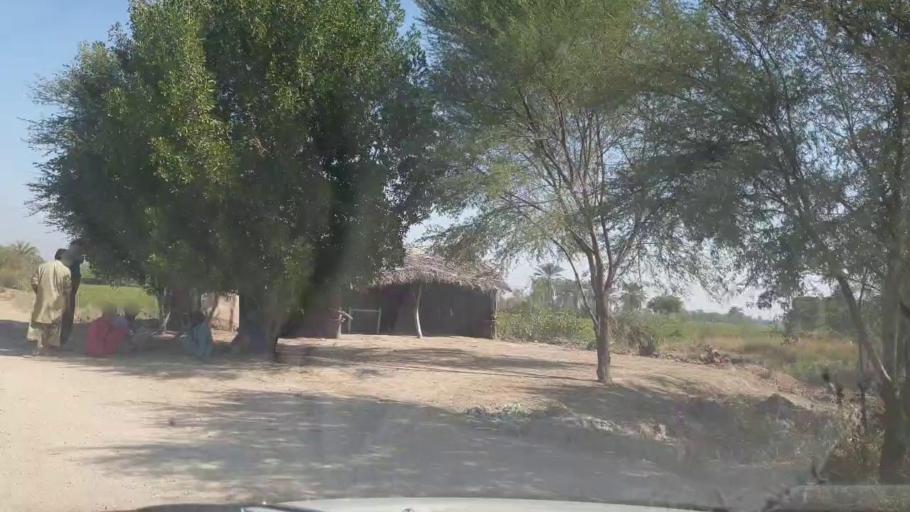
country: PK
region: Sindh
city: Mirpur Khas
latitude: 25.5139
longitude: 69.1623
